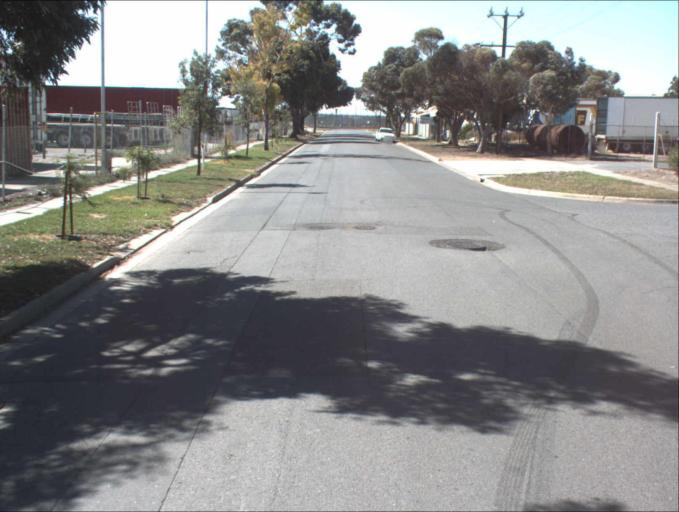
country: AU
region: South Australia
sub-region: Port Adelaide Enfield
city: Enfield
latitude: -34.8369
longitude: 138.5861
